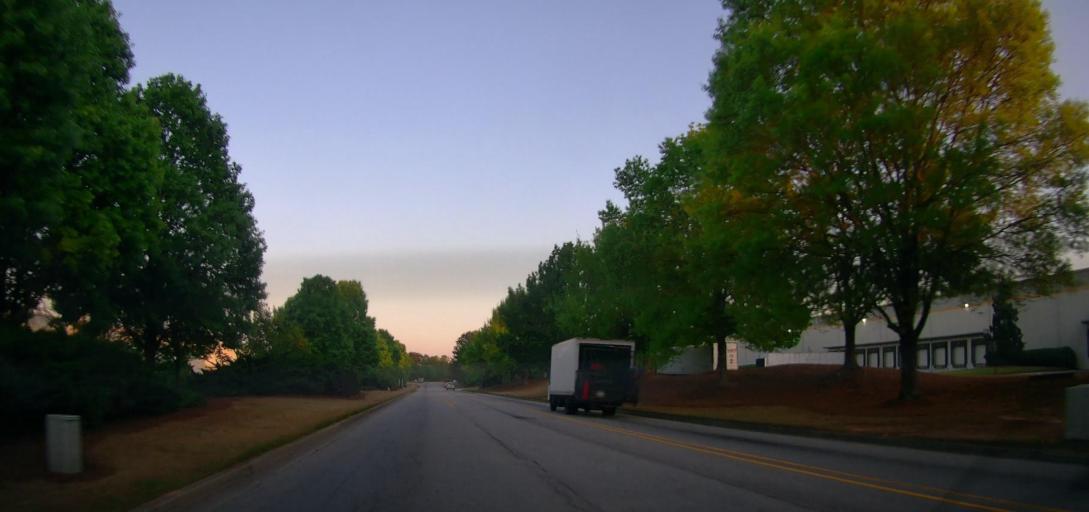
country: US
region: Georgia
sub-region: Henry County
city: McDonough
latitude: 33.4109
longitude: -84.1525
